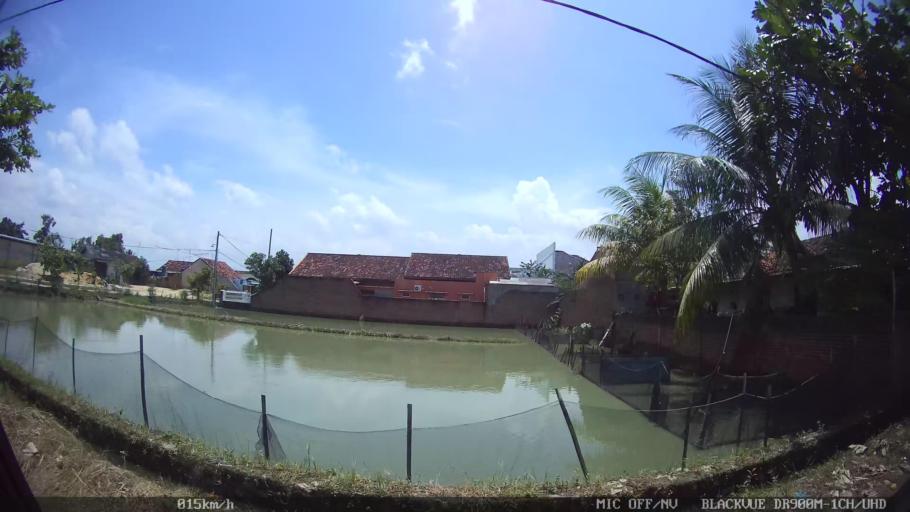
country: ID
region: Lampung
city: Kedaton
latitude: -5.3725
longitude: 105.2889
